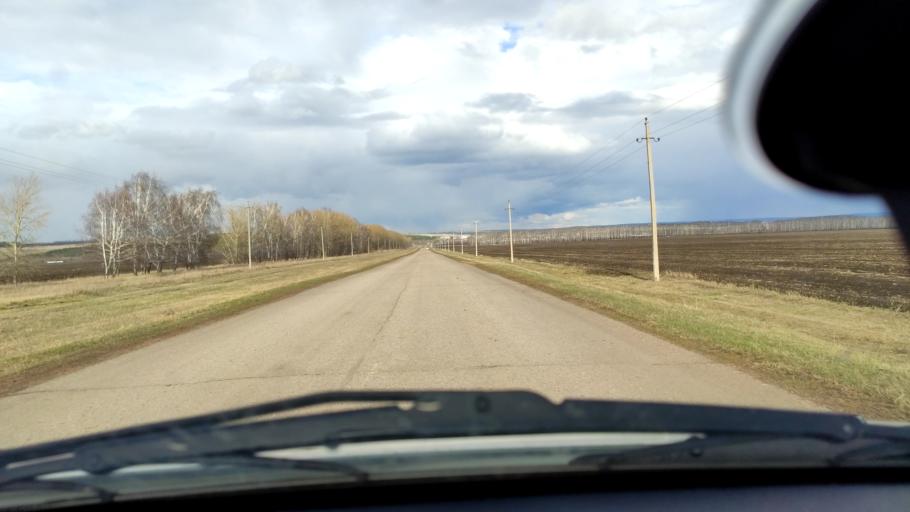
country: RU
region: Bashkortostan
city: Buzdyak
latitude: 54.7591
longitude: 54.5659
